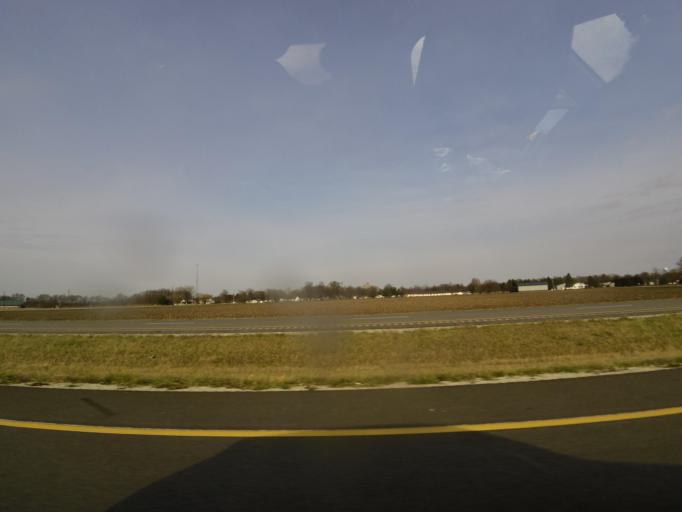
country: US
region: Illinois
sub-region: Shelby County
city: Moweaqua
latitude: 39.6149
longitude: -89.0162
